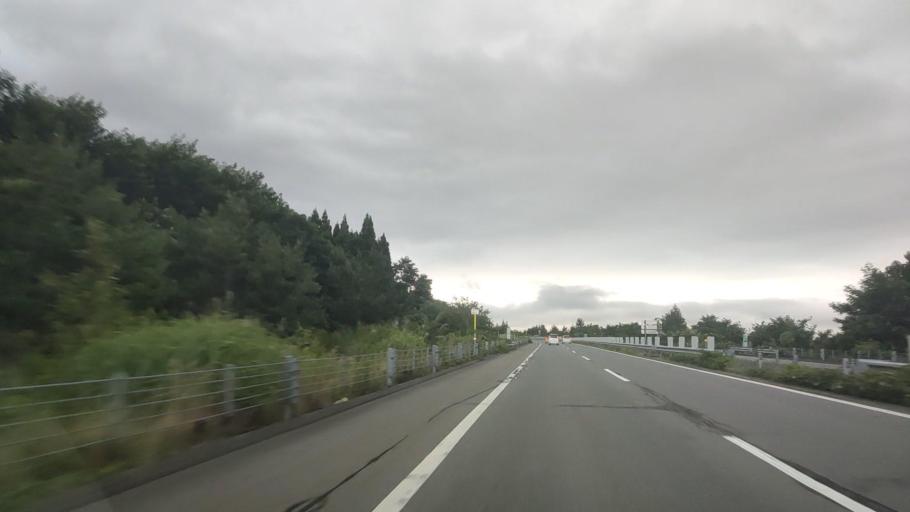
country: JP
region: Hokkaido
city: Nanae
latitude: 41.9061
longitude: 140.6972
